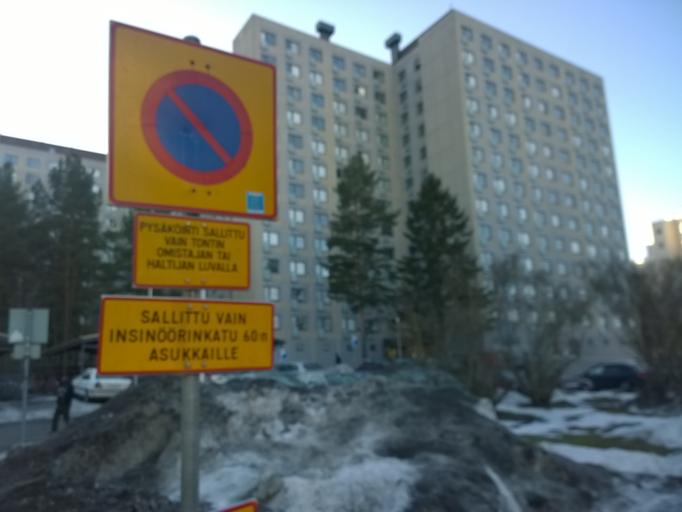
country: FI
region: Pirkanmaa
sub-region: Tampere
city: Tampere
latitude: 61.4464
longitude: 23.8541
